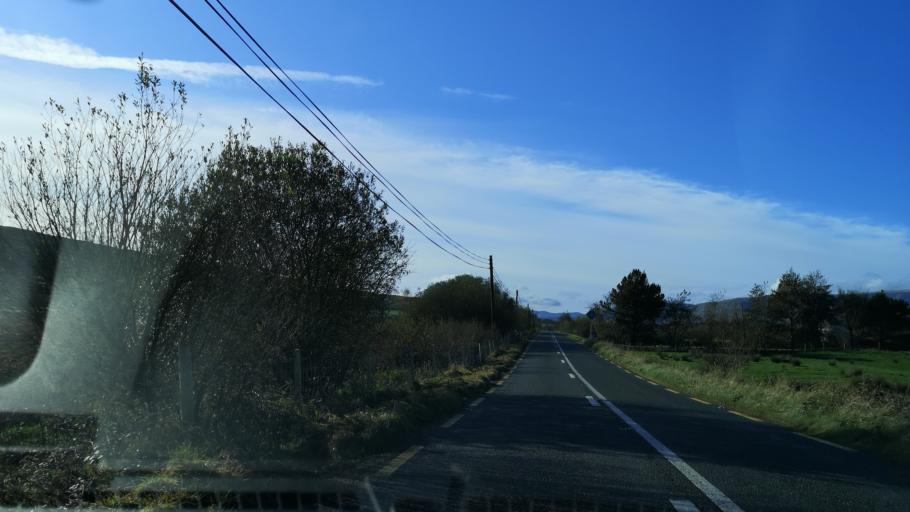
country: IE
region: Connaught
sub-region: Maigh Eo
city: Westport
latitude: 53.7201
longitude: -9.5414
